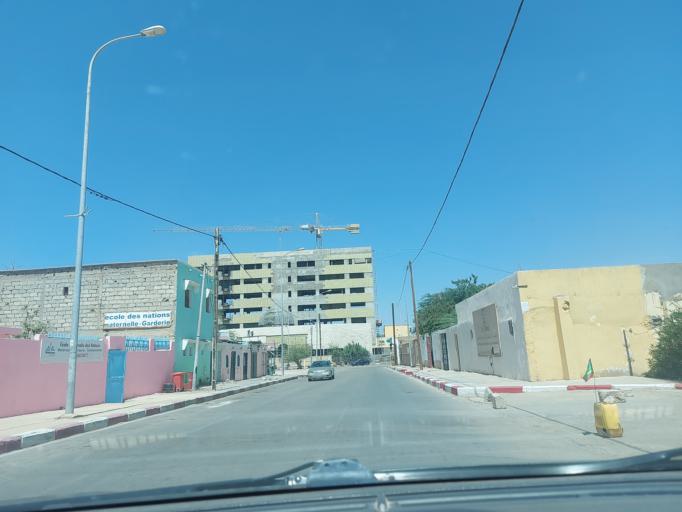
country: MR
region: Nouakchott
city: Nouakchott
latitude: 18.0930
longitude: -15.9784
